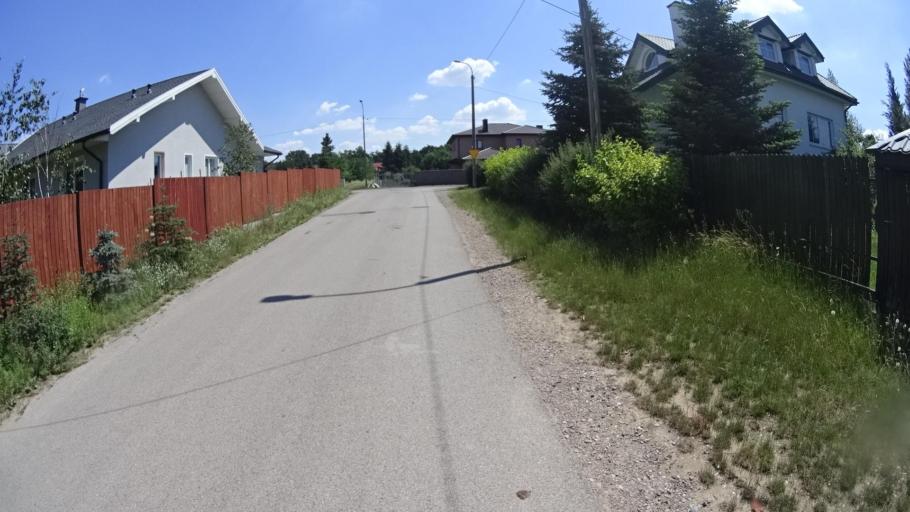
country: PL
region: Masovian Voivodeship
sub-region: Powiat warszawski zachodni
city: Babice
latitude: 52.2591
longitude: 20.8487
